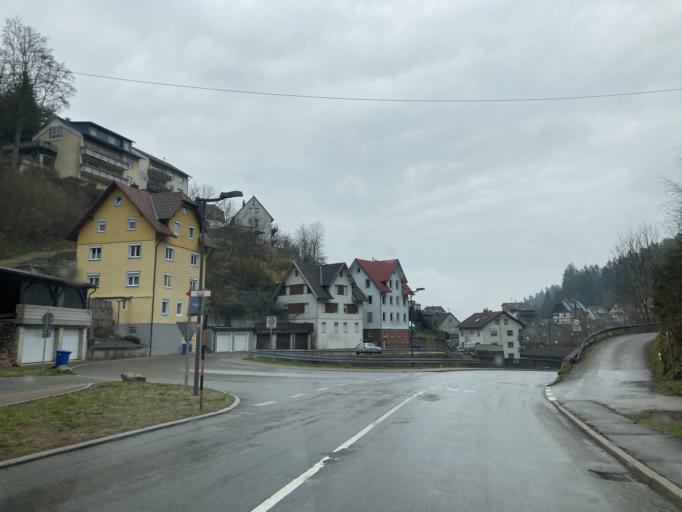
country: DE
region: Baden-Wuerttemberg
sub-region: Freiburg Region
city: Lauterbach/Schwarzwald
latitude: 48.2285
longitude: 8.3368
